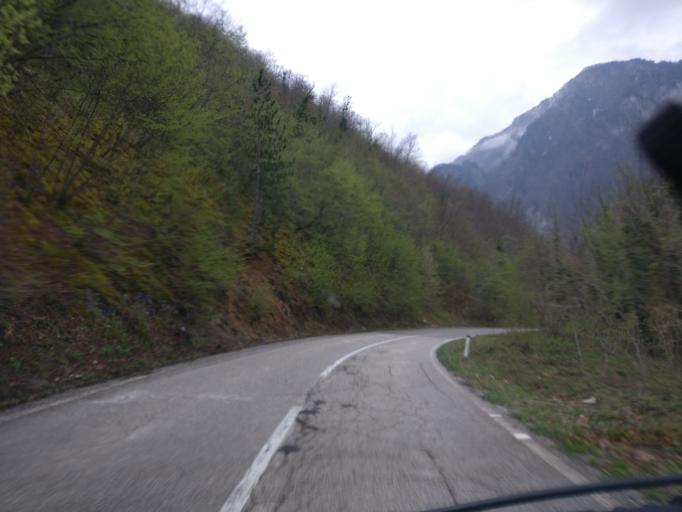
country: ME
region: Opstina Pluzine
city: Pluzine
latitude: 43.3130
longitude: 18.8562
